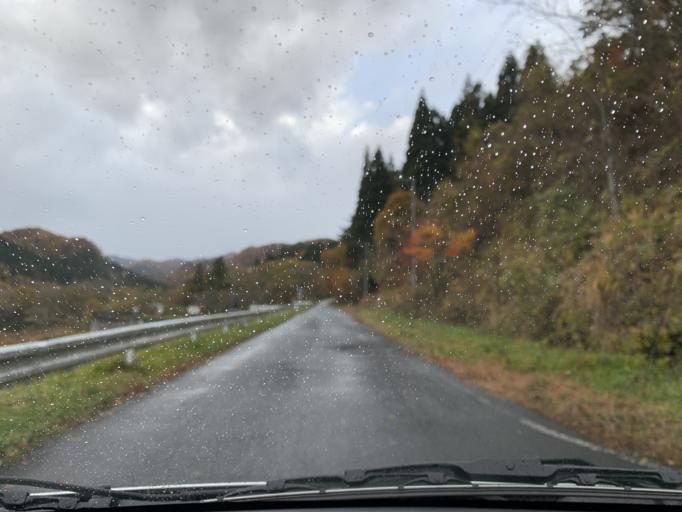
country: JP
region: Iwate
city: Mizusawa
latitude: 39.1010
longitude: 140.9667
